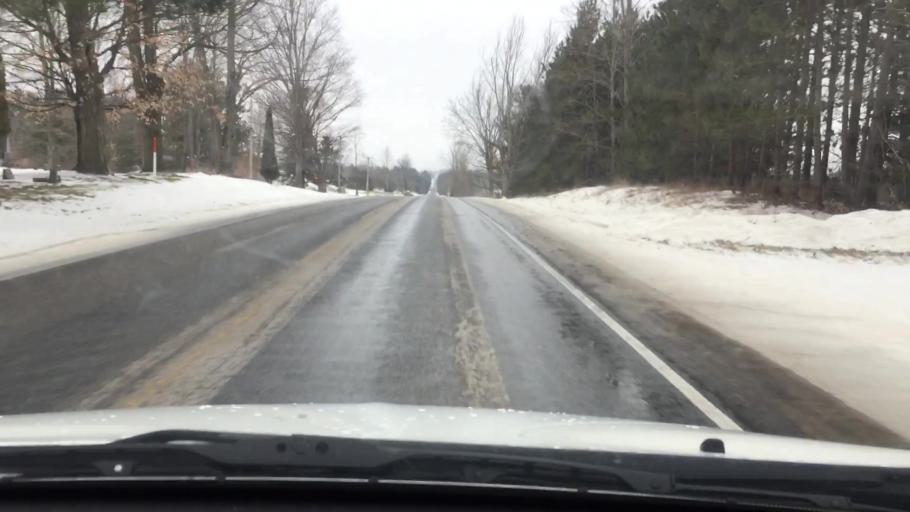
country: US
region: Michigan
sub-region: Wexford County
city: Cadillac
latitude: 44.0668
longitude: -85.4440
